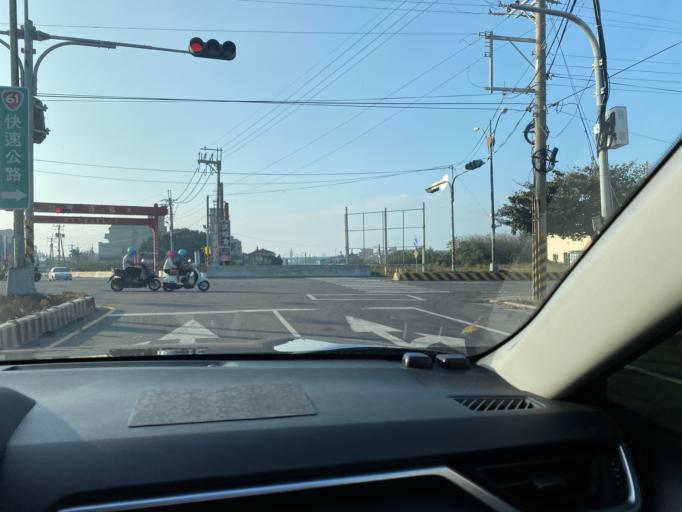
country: TW
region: Taiwan
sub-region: Changhua
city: Chang-hua
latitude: 23.9644
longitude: 120.3469
